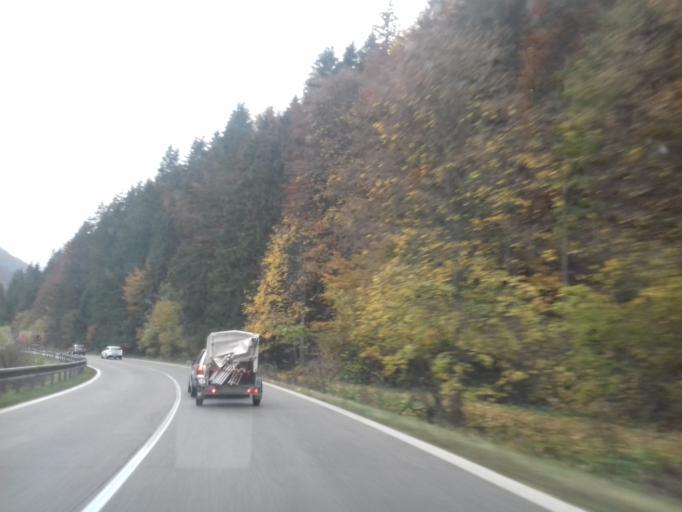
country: SK
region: Zilinsky
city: Ruzomberok
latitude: 48.9123
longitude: 19.2645
